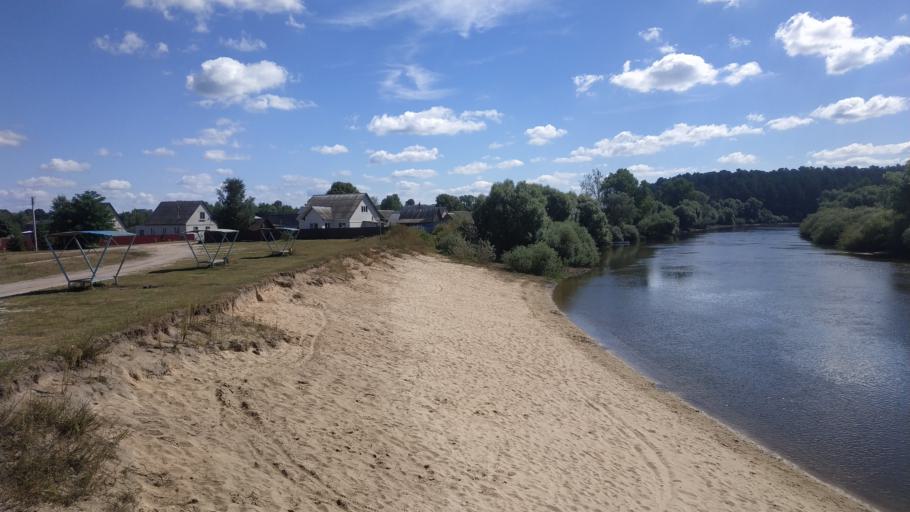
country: RU
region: Brjansk
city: Zhukovka
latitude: 53.5455
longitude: 33.6963
